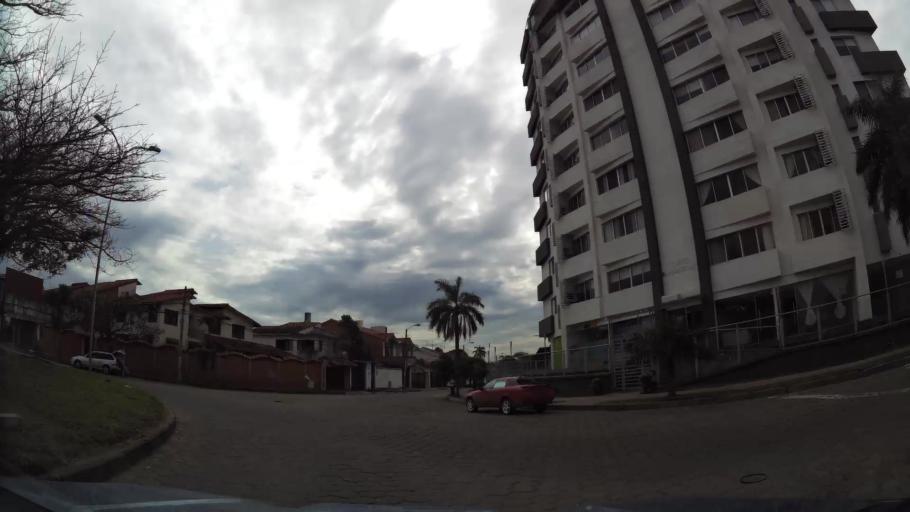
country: BO
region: Santa Cruz
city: Santa Cruz de la Sierra
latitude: -17.7998
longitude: -63.1974
